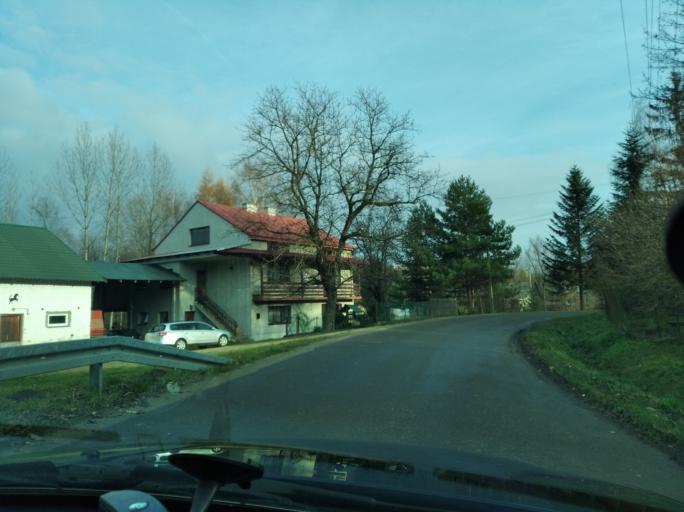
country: PL
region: Subcarpathian Voivodeship
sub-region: Powiat przeworski
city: Siedleczka
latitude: 49.9648
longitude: 22.3732
